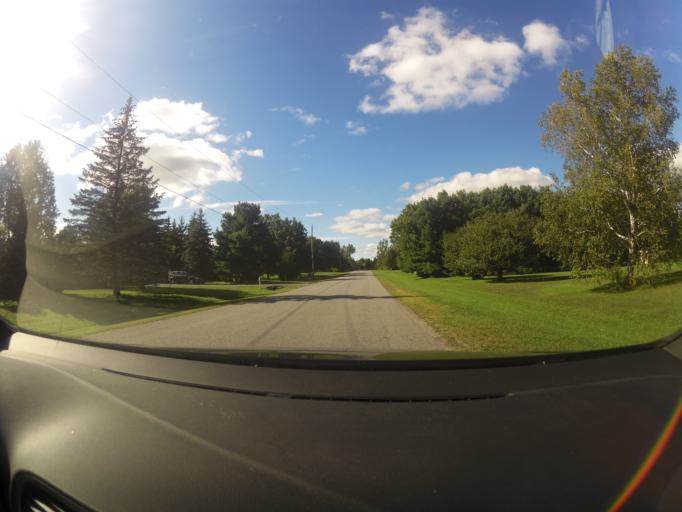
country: CA
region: Ontario
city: Carleton Place
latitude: 45.1420
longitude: -76.0798
